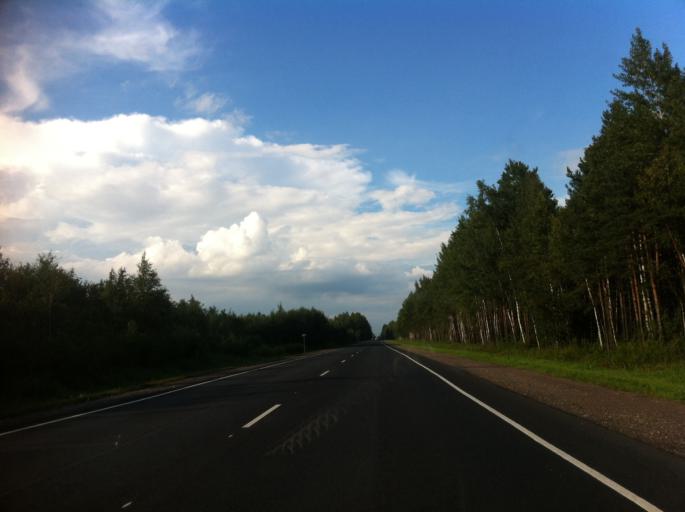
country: RU
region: Leningrad
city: Luga
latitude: 58.4525
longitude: 29.7589
